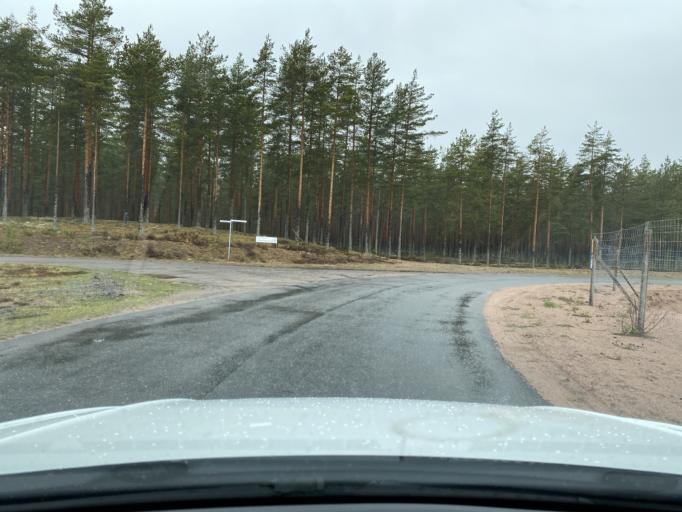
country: FI
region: Satakunta
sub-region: Pori
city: Vampula
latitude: 60.9706
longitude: 22.6597
